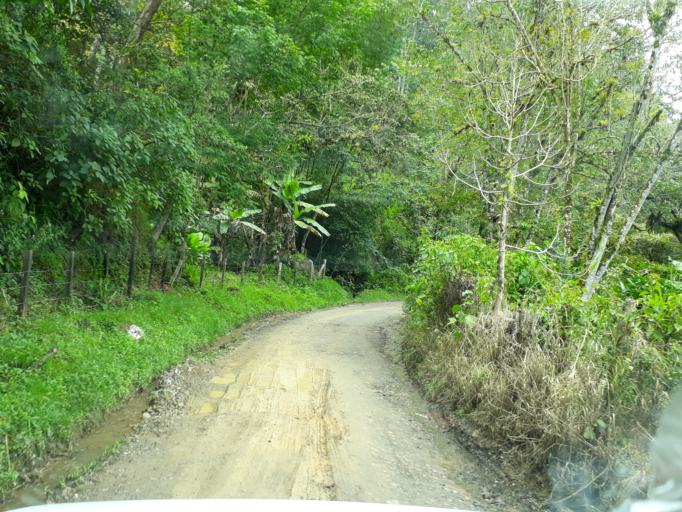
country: CO
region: Cundinamarca
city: Gacheta
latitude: 4.8447
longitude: -73.6482
